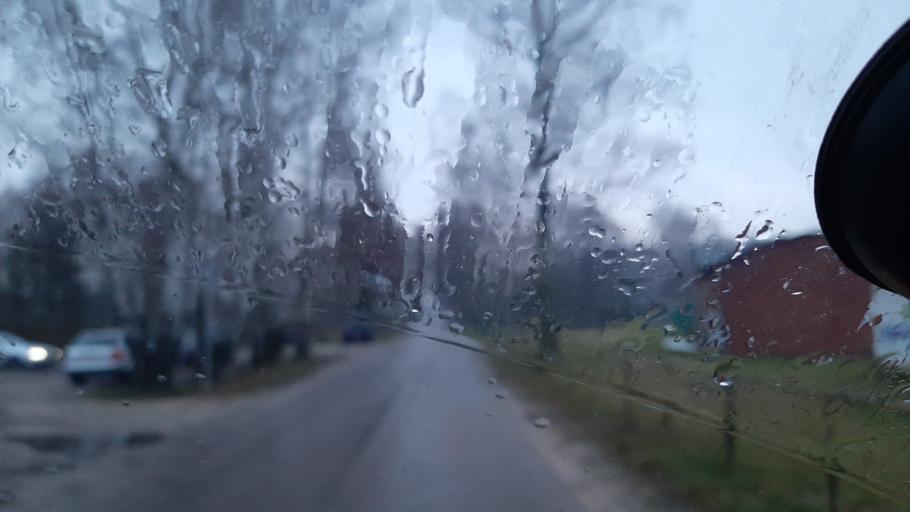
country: PL
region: Lublin Voivodeship
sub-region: Powiat lubartowski
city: Firlej
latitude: 51.5571
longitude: 22.5242
